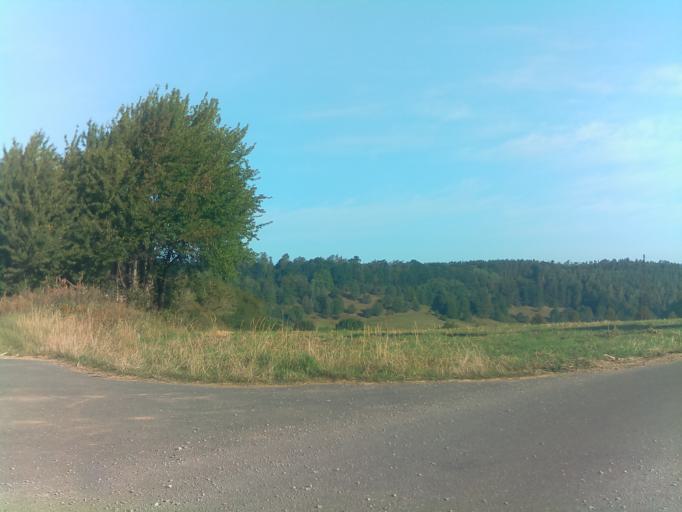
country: DE
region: Thuringia
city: Pennewitz
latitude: 50.6572
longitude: 11.0667
